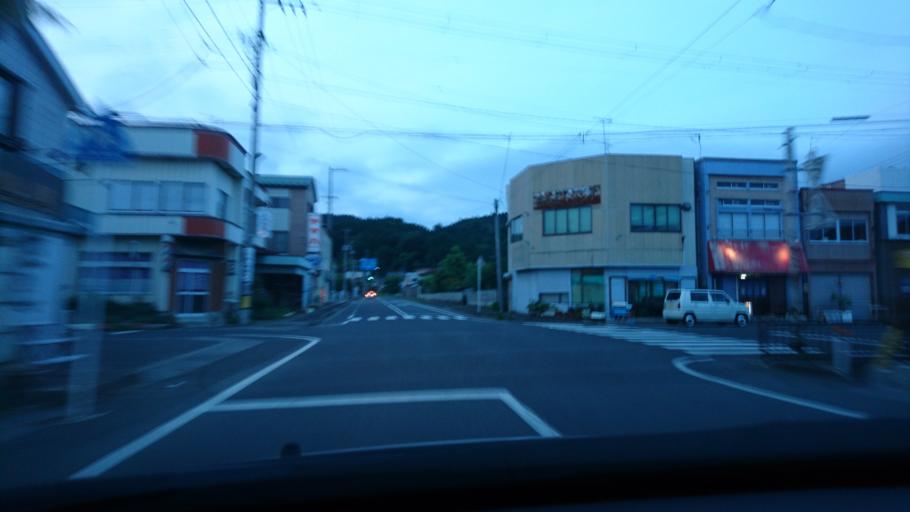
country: JP
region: Iwate
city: Ichinoseki
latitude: 38.8313
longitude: 140.9869
